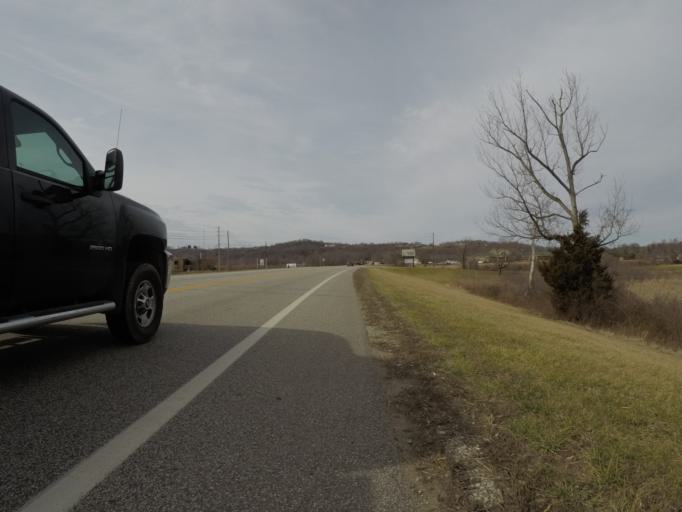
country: US
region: West Virginia
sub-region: Cabell County
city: Huntington
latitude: 38.4398
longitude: -82.3904
